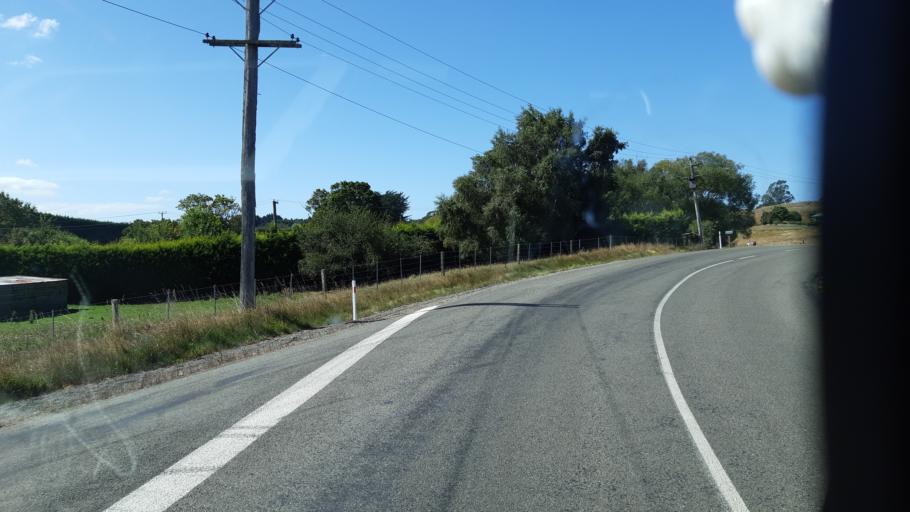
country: NZ
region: Otago
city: Oamaru
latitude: -45.0696
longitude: 170.9530
